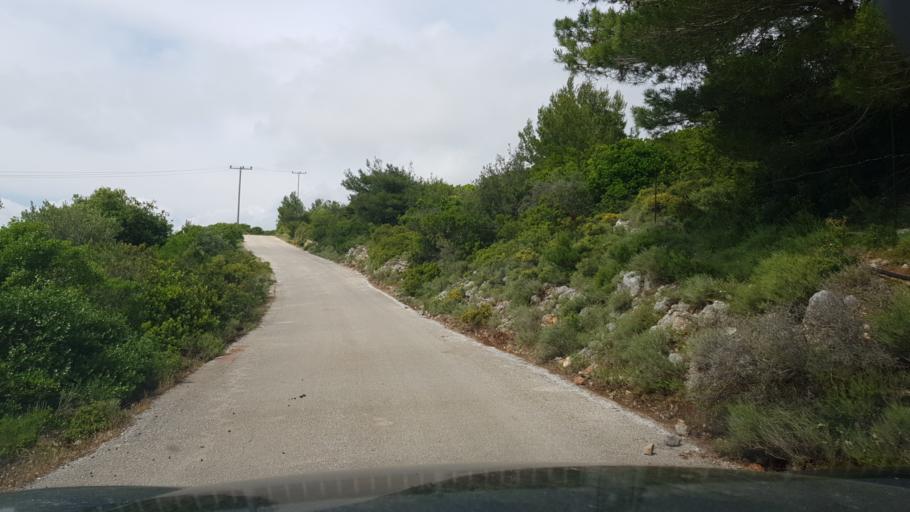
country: GR
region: Ionian Islands
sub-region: Lefkada
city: Nidri
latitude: 38.6133
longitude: 20.5648
